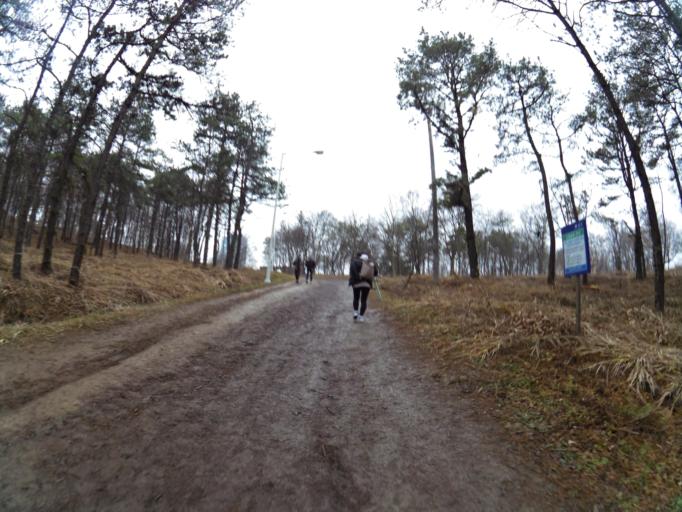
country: KR
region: Gyeongsangbuk-do
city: Gyeongsan-si
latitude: 35.8364
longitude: 128.7574
